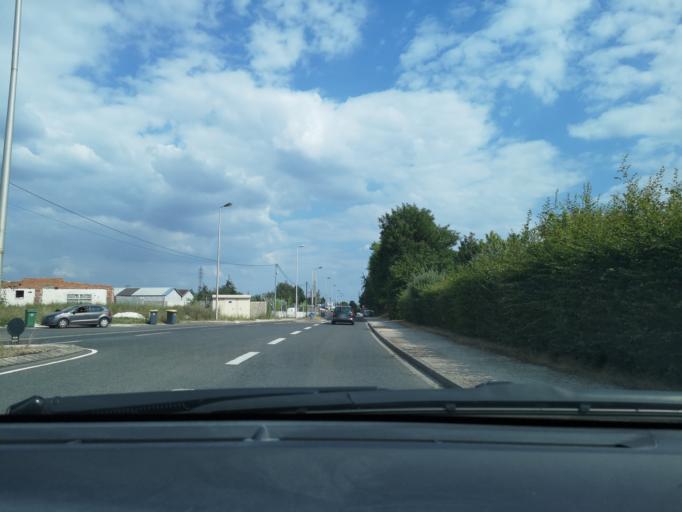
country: FR
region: Centre
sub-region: Departement du Loiret
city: Fleury-les-Aubrais
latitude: 47.9413
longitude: 1.9328
